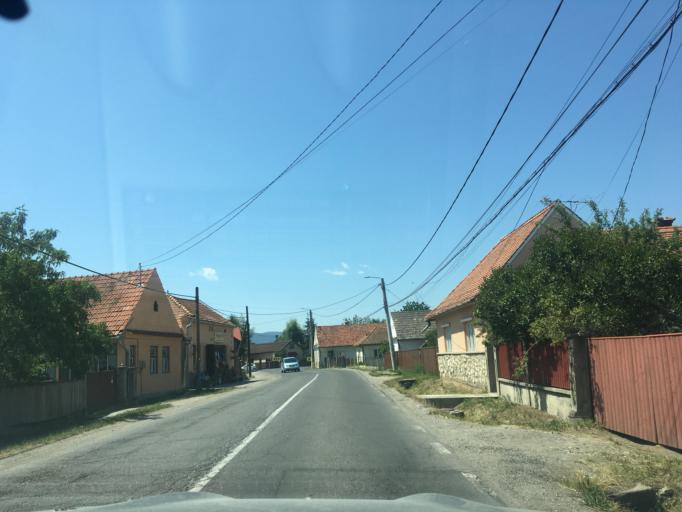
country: RO
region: Harghita
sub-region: Comuna Joseni
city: Joseni
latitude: 46.7019
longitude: 25.4974
